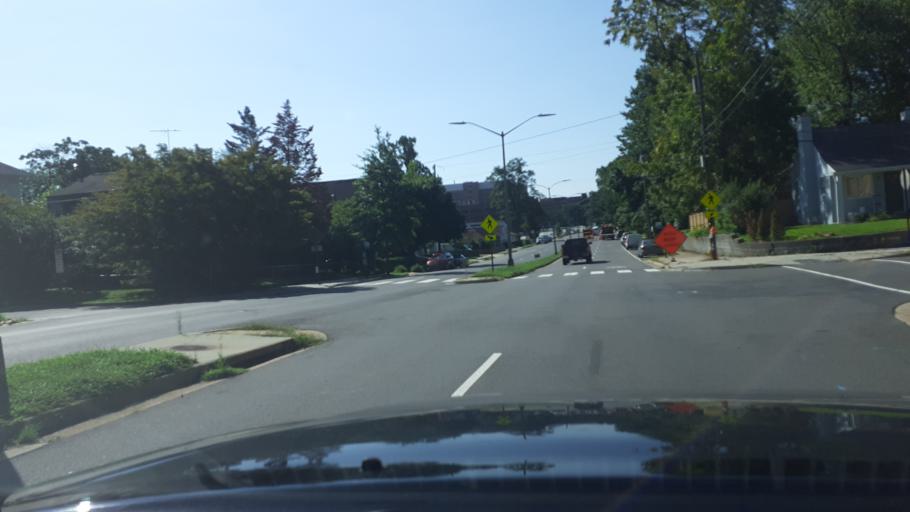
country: US
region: Virginia
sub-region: Arlington County
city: Arlington
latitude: 38.8931
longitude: -77.1309
